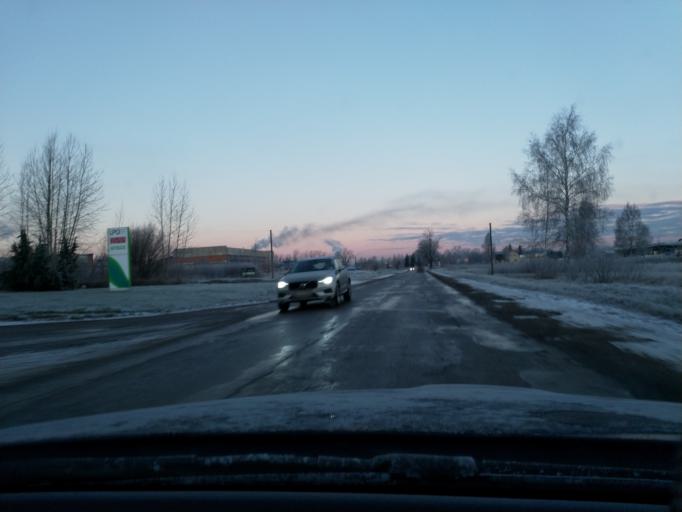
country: LV
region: Kuldigas Rajons
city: Kuldiga
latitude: 56.9539
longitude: 21.9922
